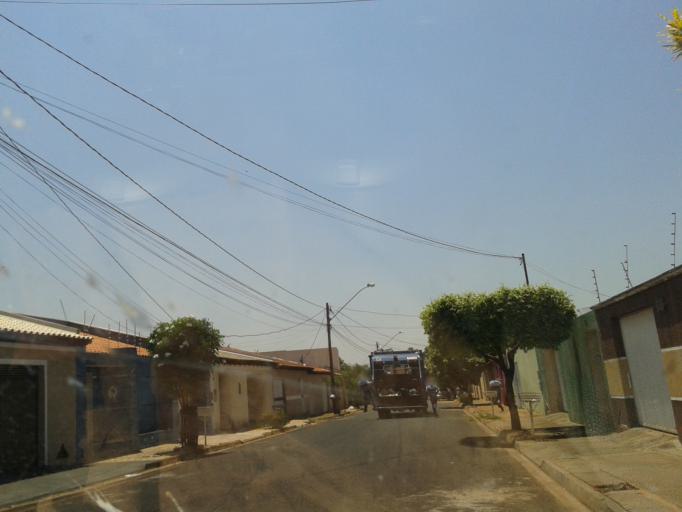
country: BR
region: Minas Gerais
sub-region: Uberlandia
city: Uberlandia
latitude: -18.9607
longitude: -48.3133
